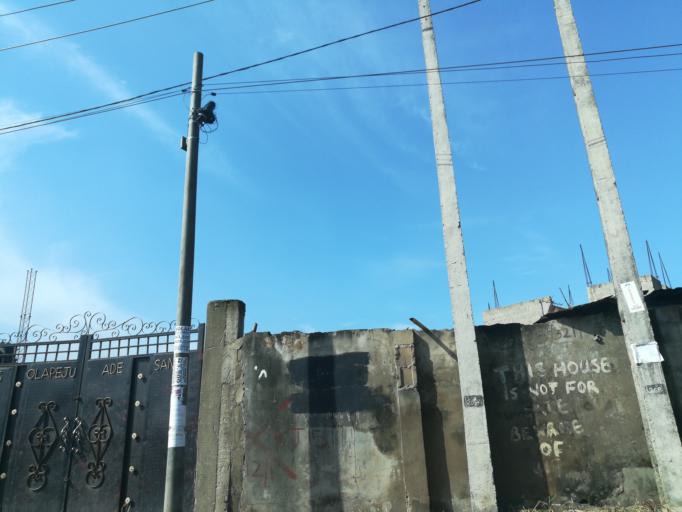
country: NG
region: Lagos
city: Ikeja
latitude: 6.6009
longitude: 3.3412
